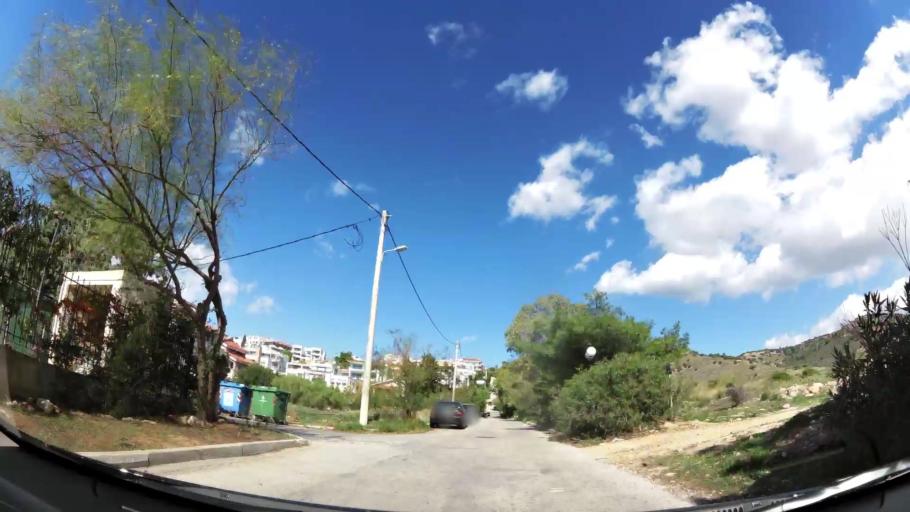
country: GR
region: Attica
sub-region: Nomarchia Anatolikis Attikis
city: Voula
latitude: 37.8428
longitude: 23.7846
